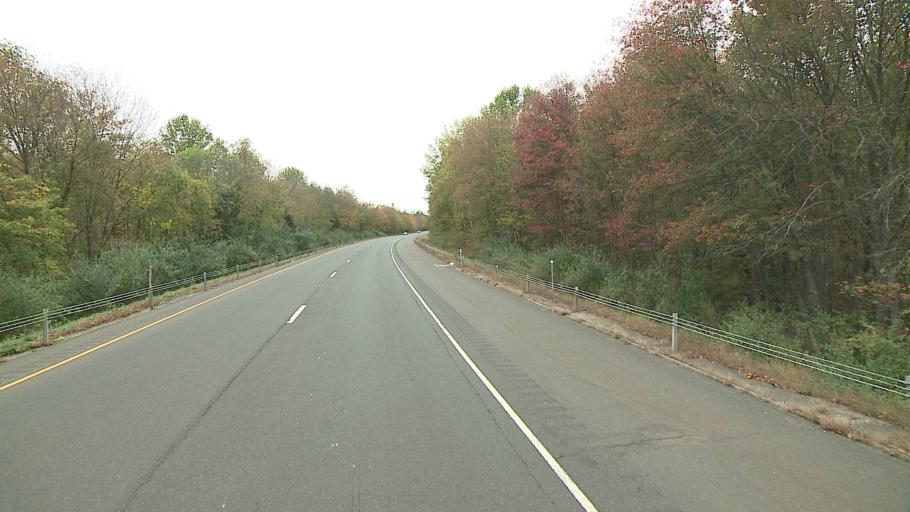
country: US
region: Connecticut
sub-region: Middlesex County
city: East Haddam
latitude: 41.4253
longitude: -72.5031
